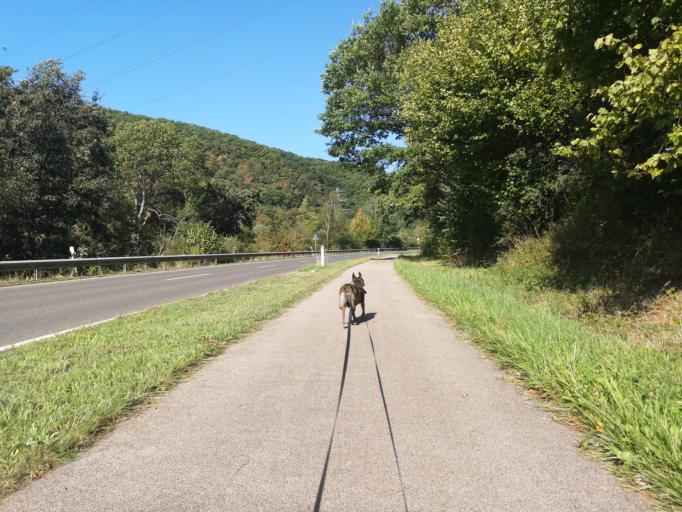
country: DE
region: North Rhine-Westphalia
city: Heimbach
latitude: 50.6478
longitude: 6.4773
